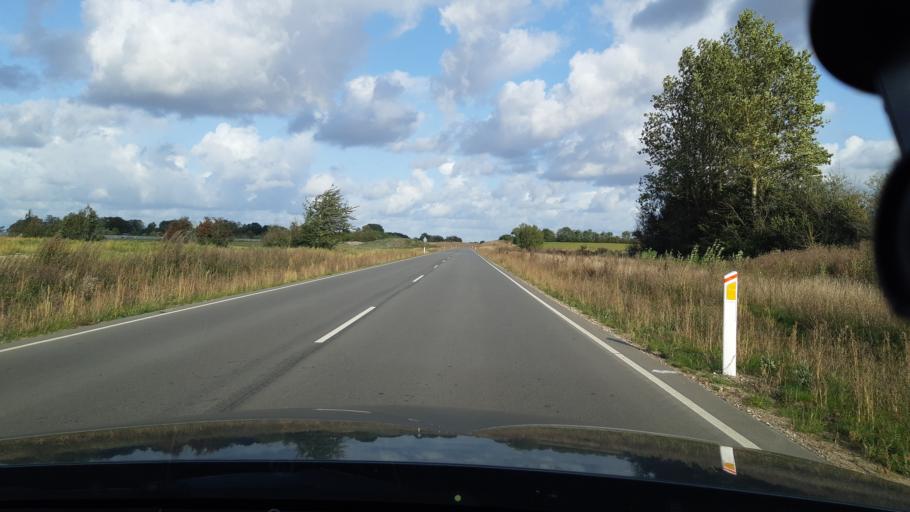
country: DK
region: Zealand
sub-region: Holbaek Kommune
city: Holbaek
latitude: 55.6563
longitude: 11.6352
